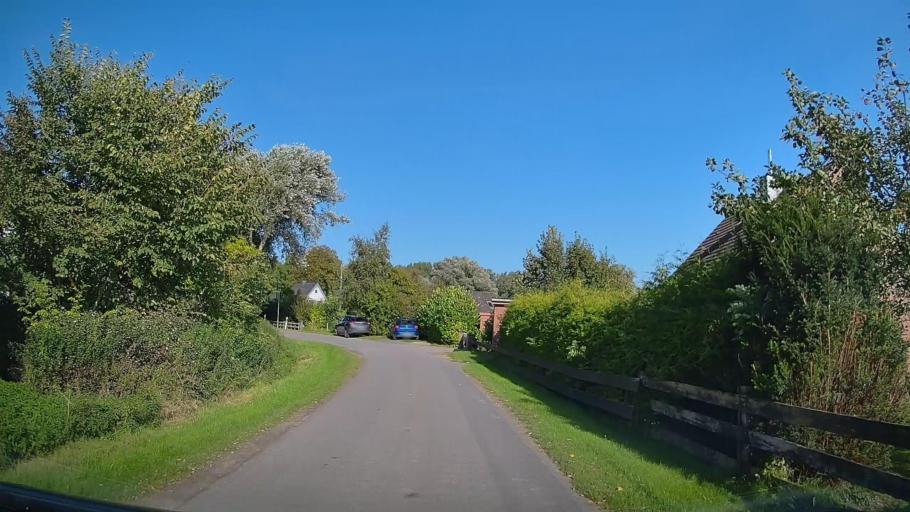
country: DE
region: Lower Saxony
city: Padingbuttel
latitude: 53.7060
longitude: 8.5032
